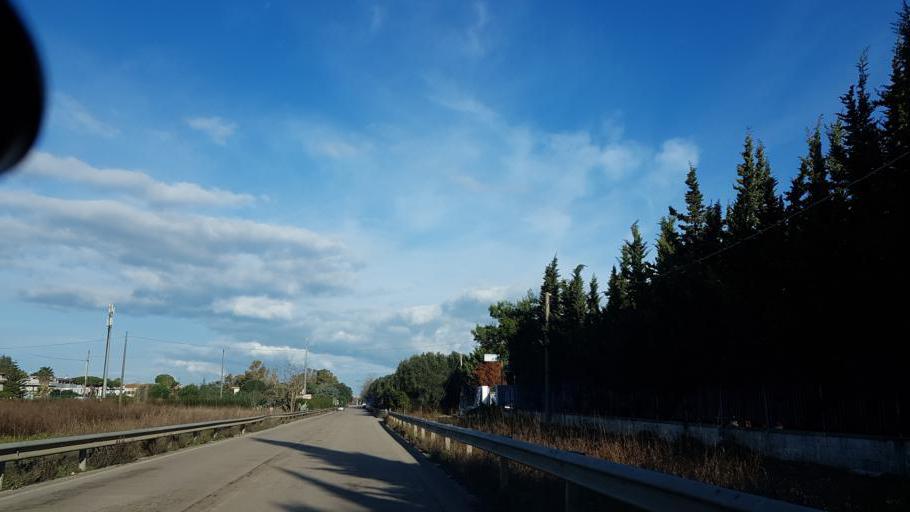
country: IT
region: Apulia
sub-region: Provincia di Brindisi
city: La Rosa
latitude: 40.6054
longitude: 17.9553
